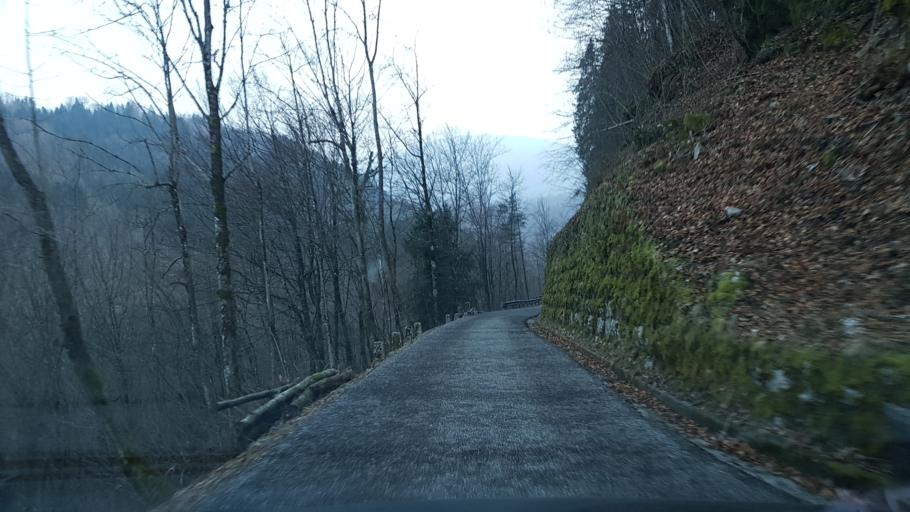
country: IT
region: Friuli Venezia Giulia
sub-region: Provincia di Udine
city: Taipana
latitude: 46.2469
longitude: 13.4035
